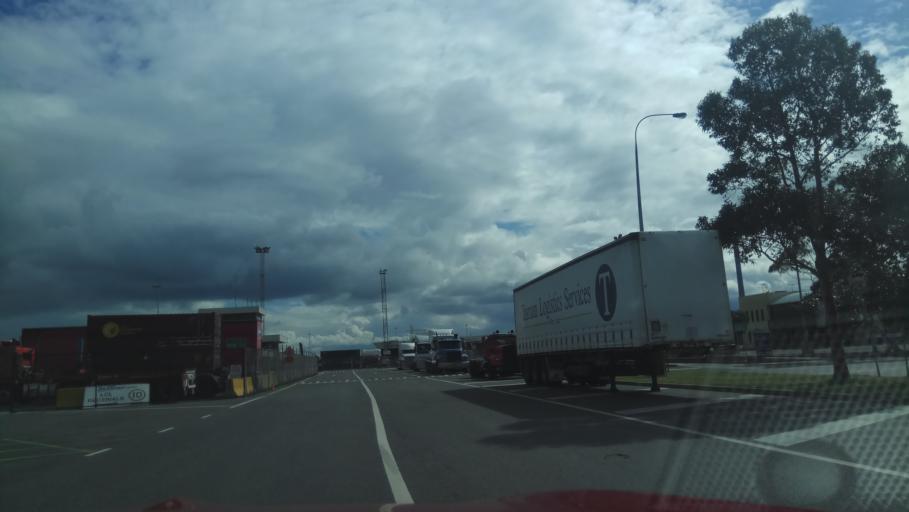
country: AU
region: Victoria
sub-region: Hobsons Bay
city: Williamstown
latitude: -37.8416
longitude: 144.9111
